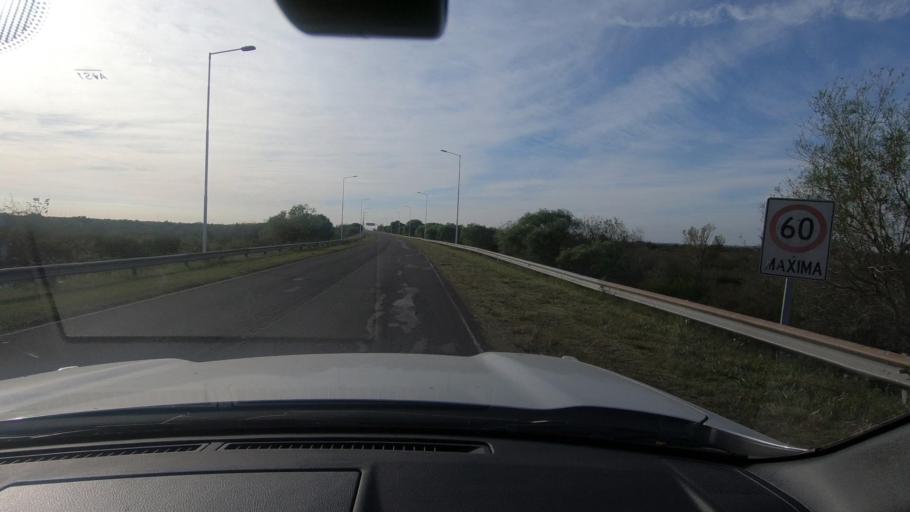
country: AR
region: Entre Rios
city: Colon
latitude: -32.2398
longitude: -58.1745
